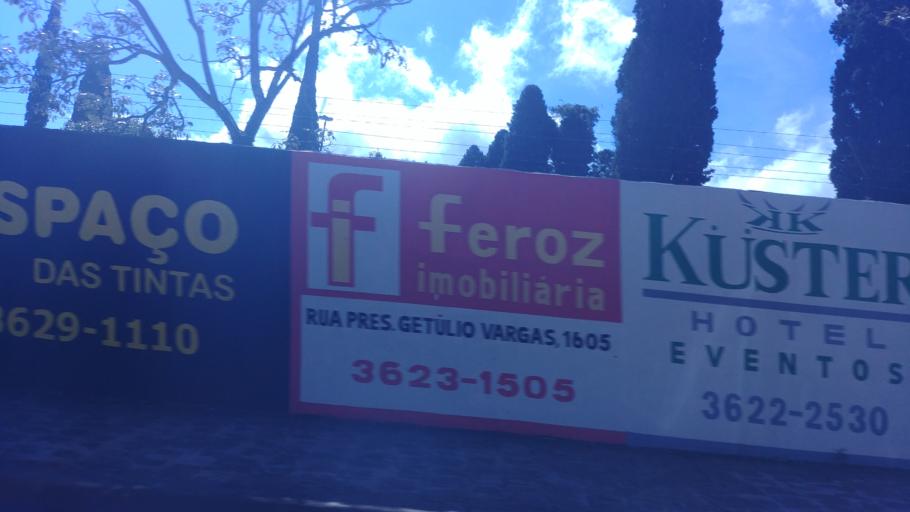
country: BR
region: Parana
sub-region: Guarapuava
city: Guarapuava
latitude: -25.3963
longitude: -51.4574
